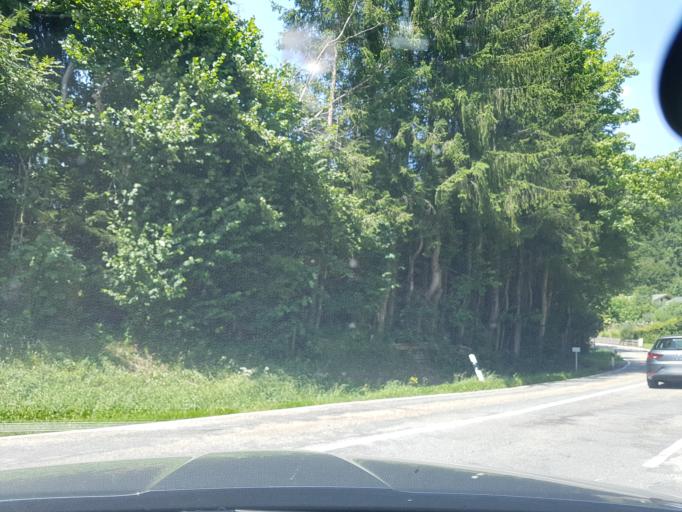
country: DE
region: Bavaria
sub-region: Upper Bavaria
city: Berchtesgaden
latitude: 47.6441
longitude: 13.0004
